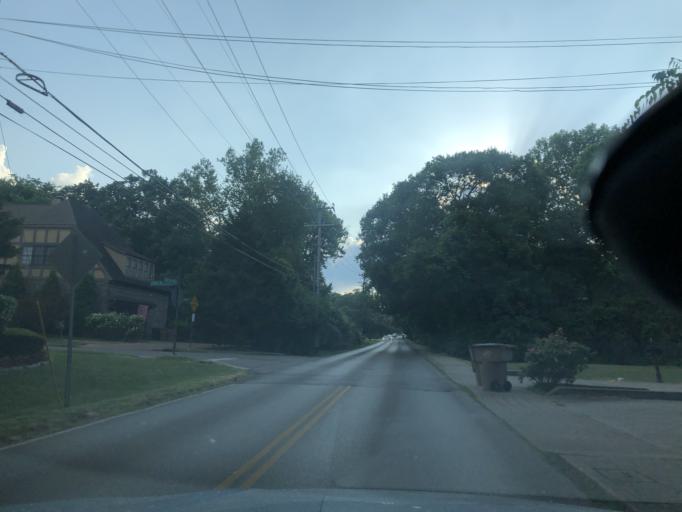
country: US
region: Tennessee
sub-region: Davidson County
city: Oak Hill
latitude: 36.1014
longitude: -86.8030
